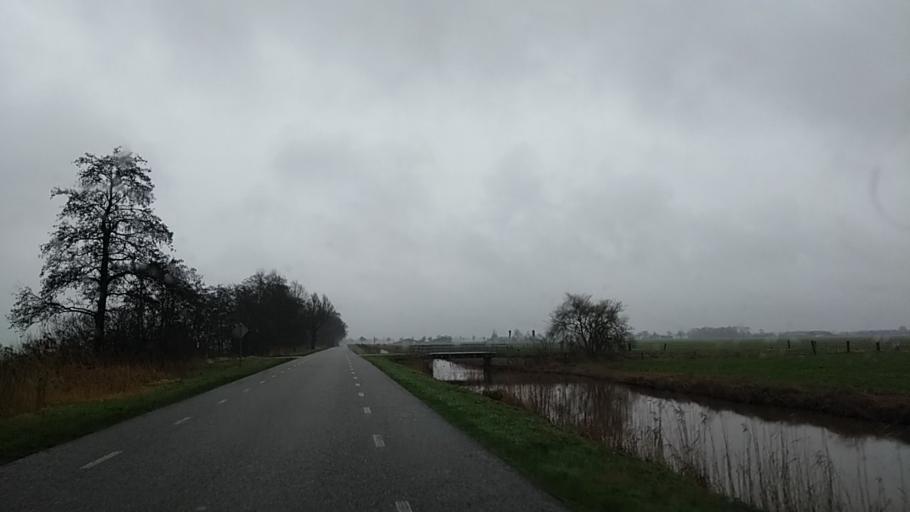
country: NL
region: Overijssel
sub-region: Gemeente Zwartewaterland
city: Hasselt
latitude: 52.6103
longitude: 6.1442
